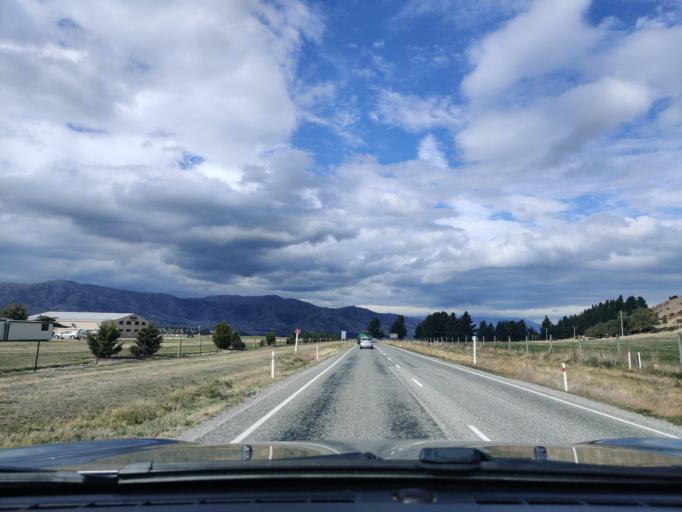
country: NZ
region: Otago
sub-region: Queenstown-Lakes District
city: Wanaka
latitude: -44.7254
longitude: 169.2454
